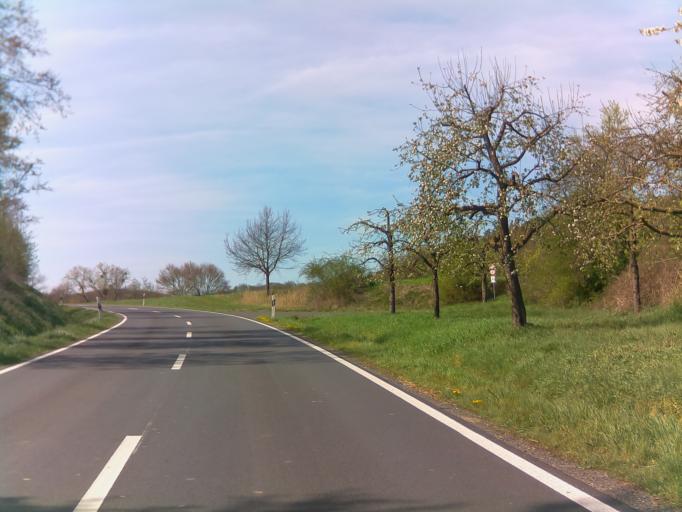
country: DE
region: Bavaria
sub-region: Regierungsbezirk Unterfranken
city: Burgpreppach
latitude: 50.1567
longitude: 10.6056
